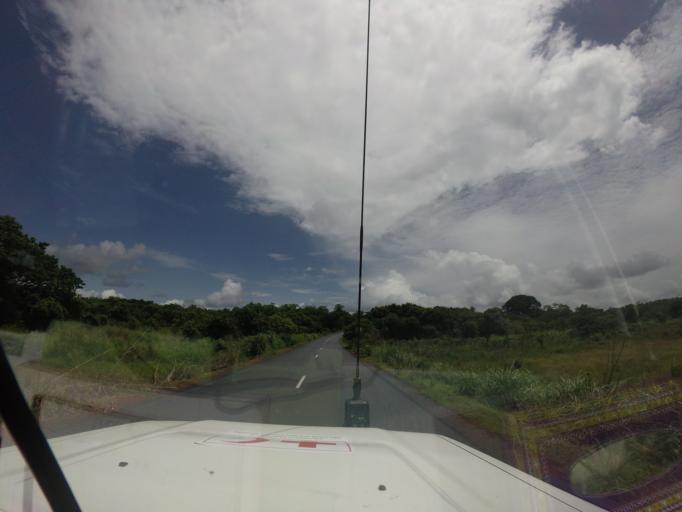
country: GN
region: Faranah
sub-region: Faranah Prefecture
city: Faranah
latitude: 10.0169
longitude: -10.8991
